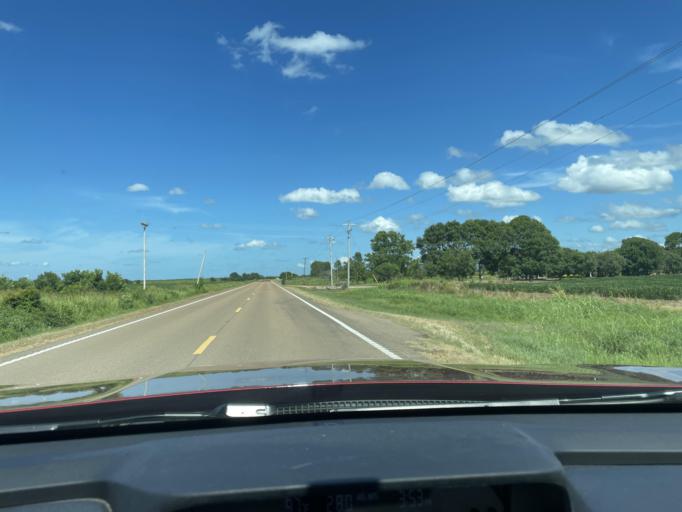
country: US
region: Mississippi
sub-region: Humphreys County
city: Belzoni
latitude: 33.1843
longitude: -90.6681
